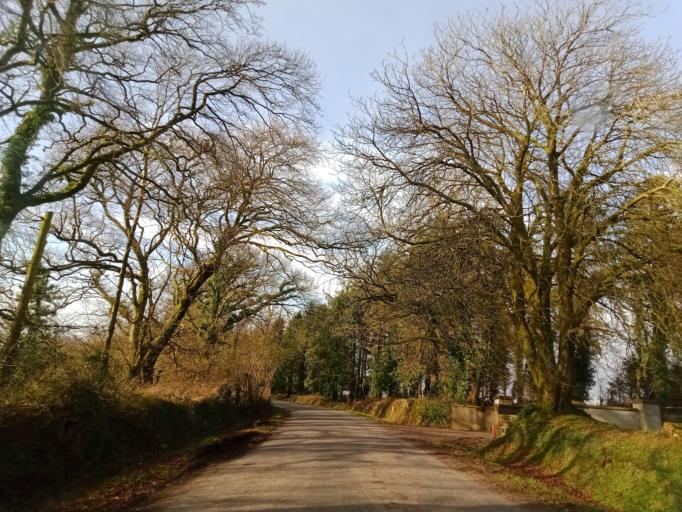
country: IE
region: Munster
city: Fethard
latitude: 52.5648
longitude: -7.6371
